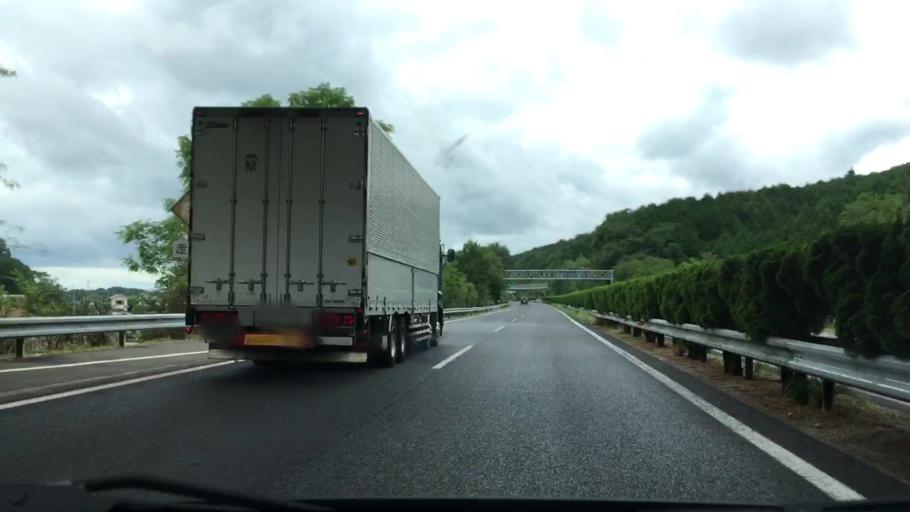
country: JP
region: Okayama
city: Tsuyama
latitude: 35.0375
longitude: 134.1314
